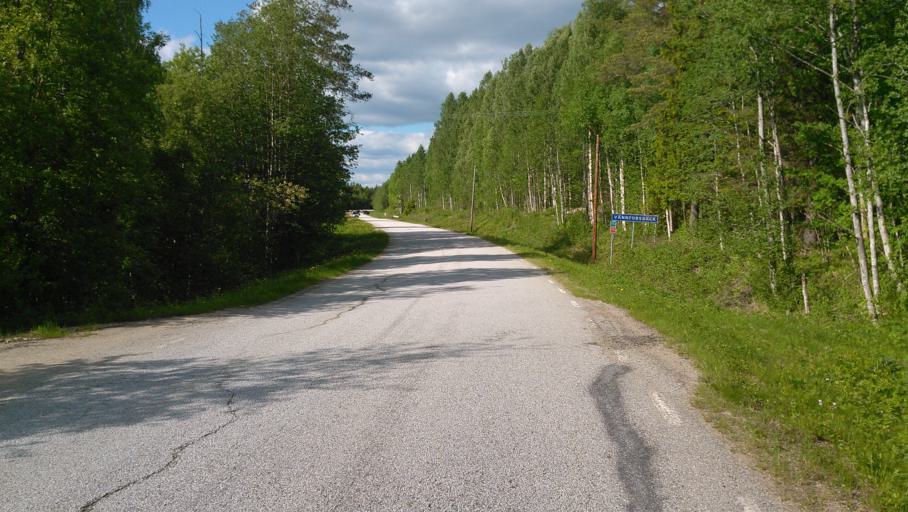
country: SE
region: Vaesterbotten
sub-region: Vannas Kommun
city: Vannasby
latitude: 64.0024
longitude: 19.9184
